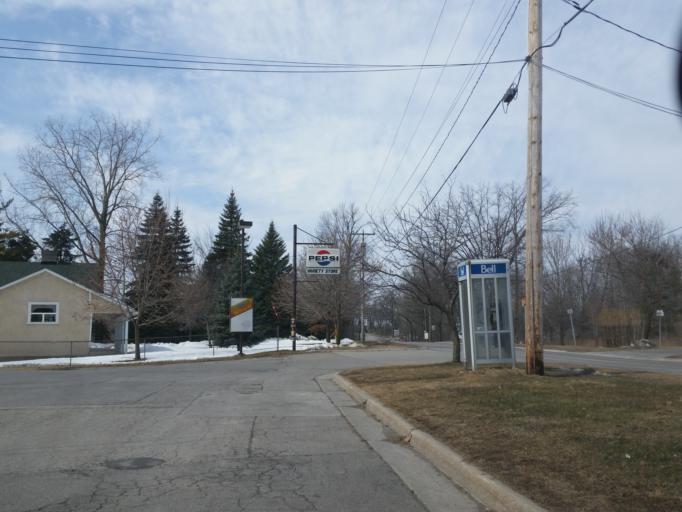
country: CA
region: Ontario
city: Deseronto
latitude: 44.1961
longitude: -77.0597
